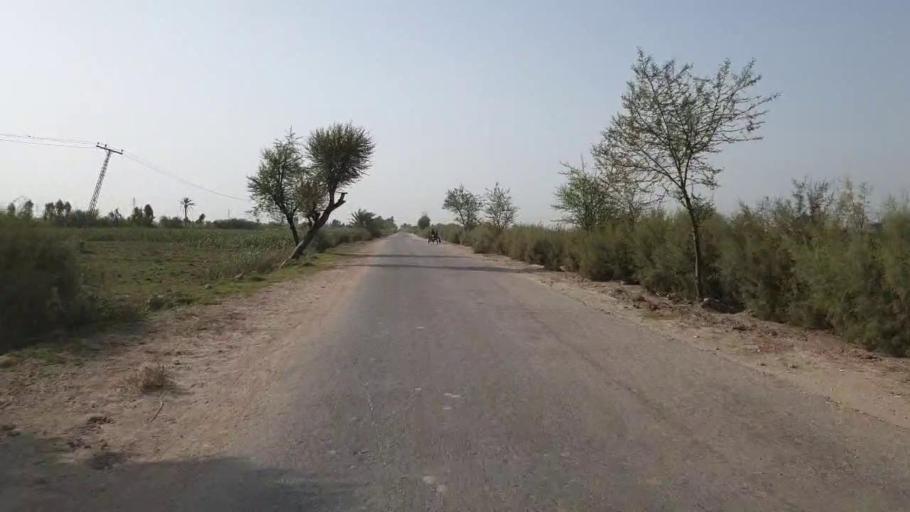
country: PK
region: Sindh
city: Khadro
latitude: 26.3282
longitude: 68.9307
